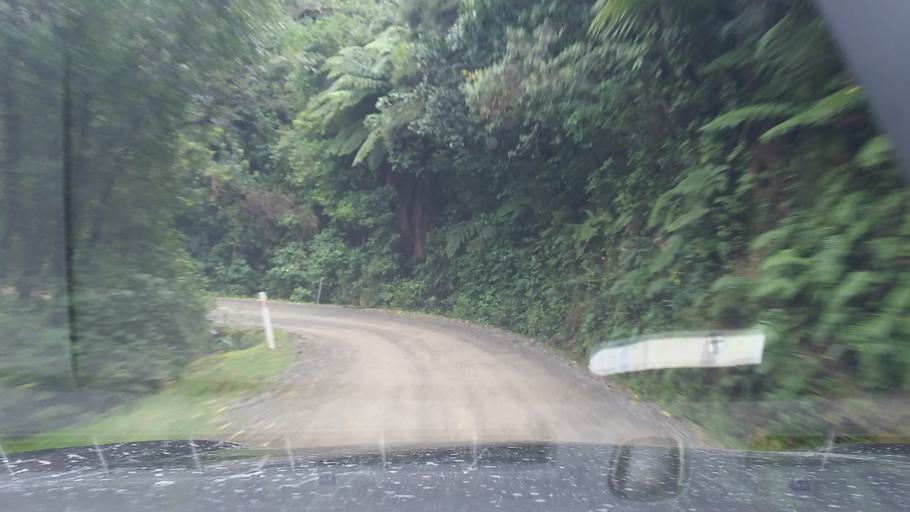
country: NZ
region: Marlborough
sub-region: Marlborough District
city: Picton
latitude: -41.1786
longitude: 173.9943
